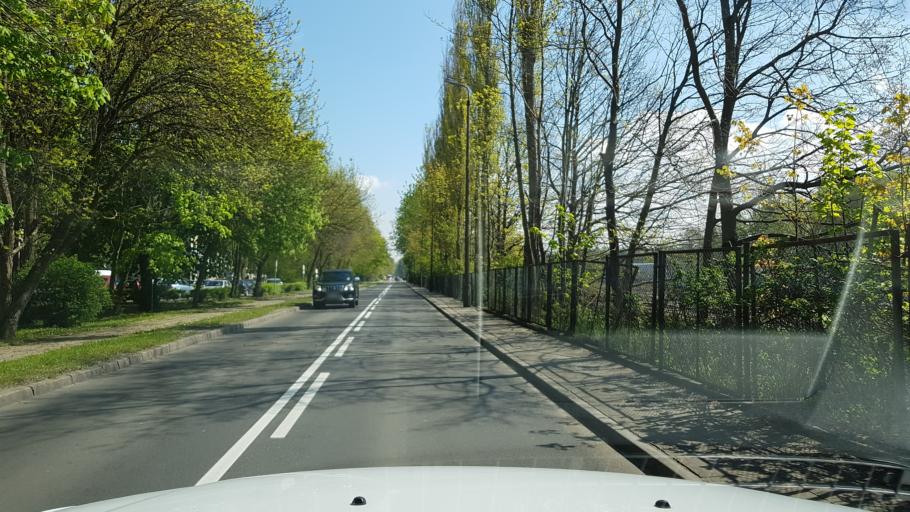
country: PL
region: Pomeranian Voivodeship
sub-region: Powiat slupski
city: Ustka
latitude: 54.5781
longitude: 16.8636
